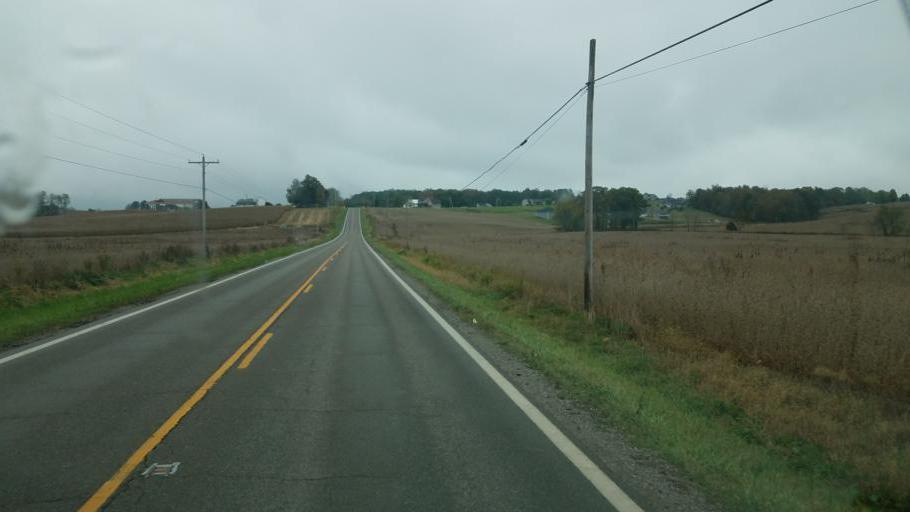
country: US
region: Ohio
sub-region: Wayne County
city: Shreve
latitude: 40.5798
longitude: -82.0387
